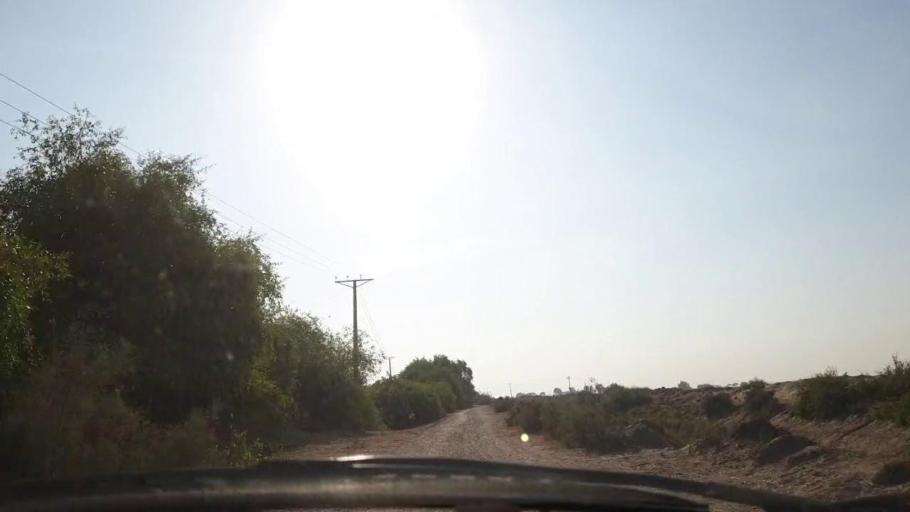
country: PK
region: Sindh
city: Bulri
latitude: 24.8168
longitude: 68.4032
